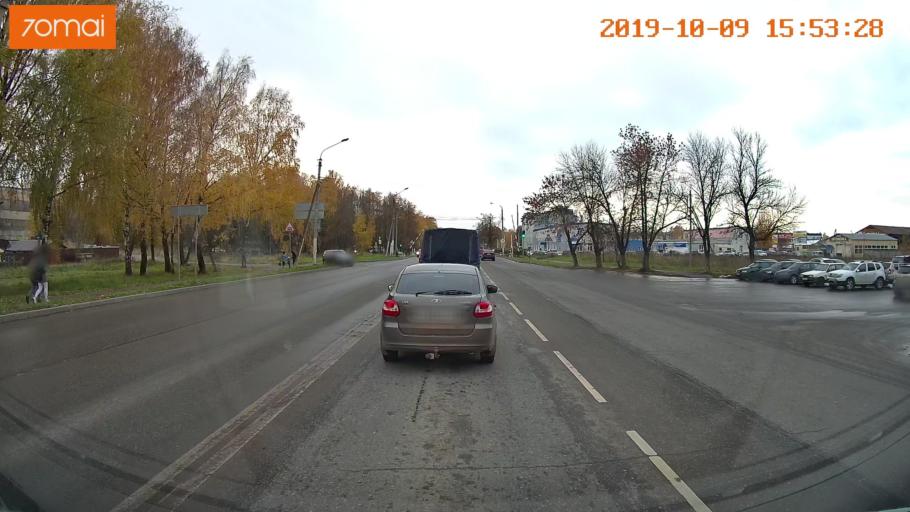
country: RU
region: Kostroma
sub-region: Kostromskoy Rayon
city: Kostroma
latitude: 57.7852
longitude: 40.9615
